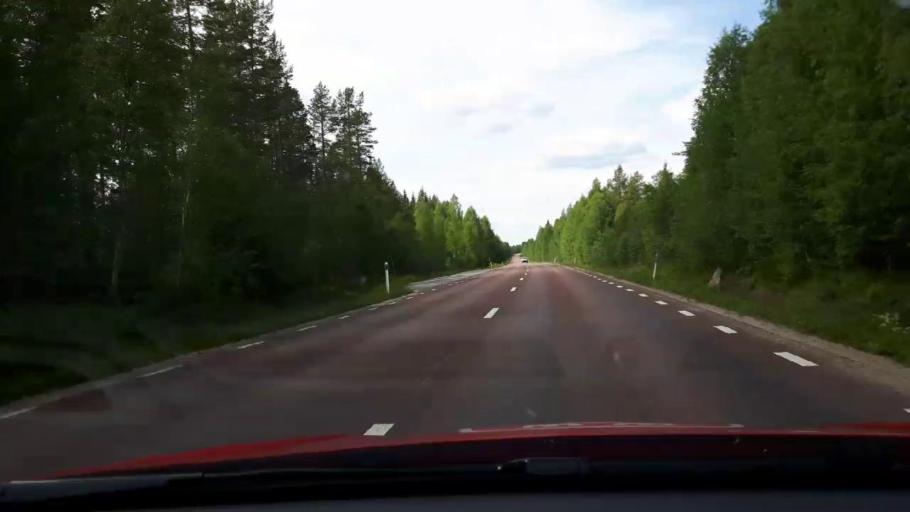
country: SE
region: Jaemtland
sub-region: Harjedalens Kommun
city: Sveg
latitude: 62.0466
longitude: 14.8349
